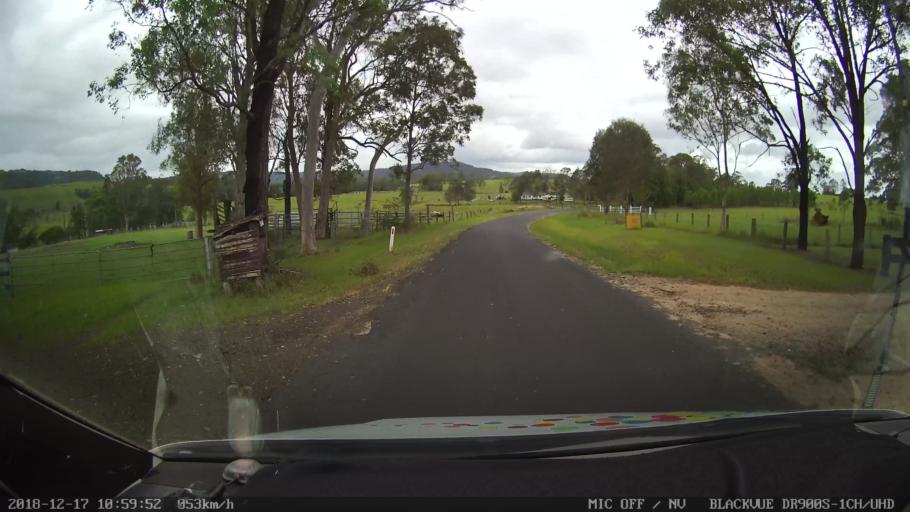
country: AU
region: New South Wales
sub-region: Richmond Valley
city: Casino
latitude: -28.8187
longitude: 152.6150
